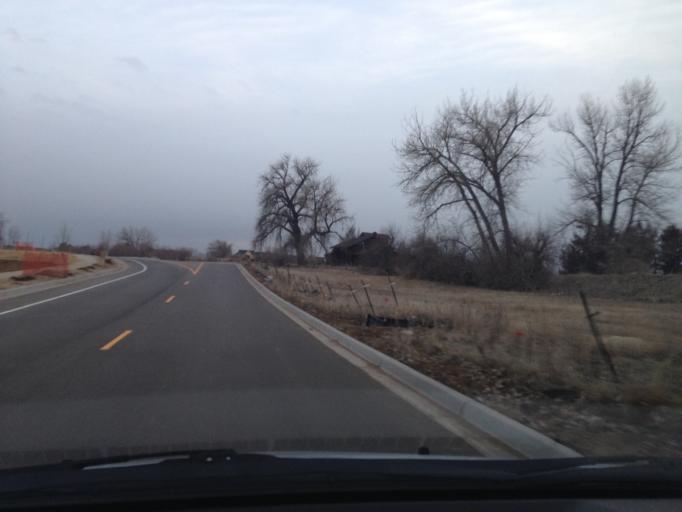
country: US
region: Colorado
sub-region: Boulder County
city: Lafayette
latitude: 40.0104
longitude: -105.1075
